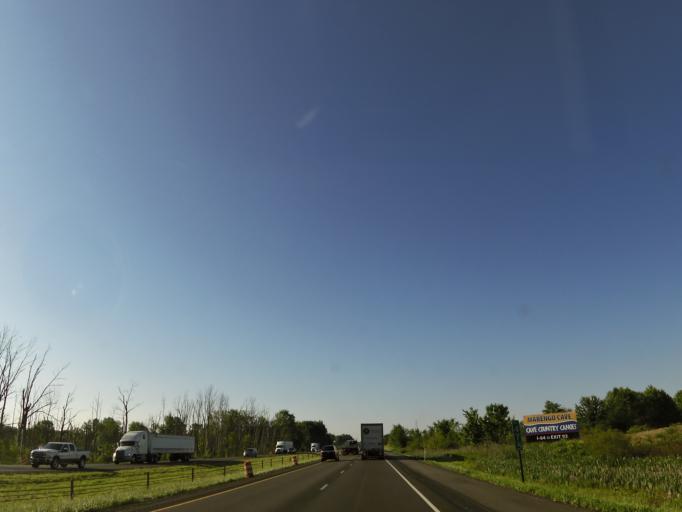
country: US
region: Indiana
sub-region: Jackson County
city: Seymour
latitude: 38.9303
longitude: -85.8403
